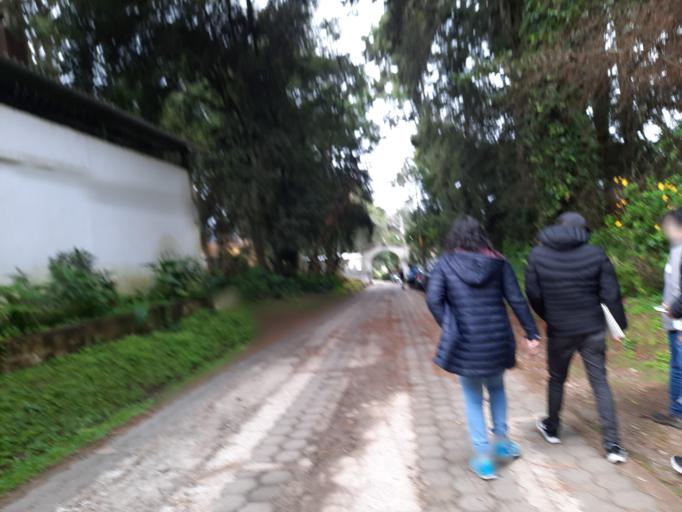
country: GT
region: Sacatepequez
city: San Lucas Sacatepequez
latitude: 14.6371
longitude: -90.6468
